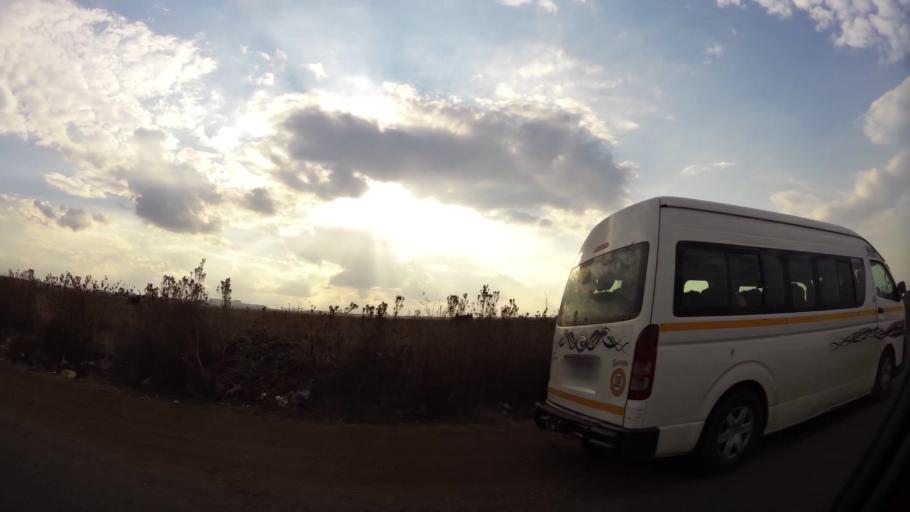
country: ZA
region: Gauteng
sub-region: Sedibeng District Municipality
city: Vereeniging
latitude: -26.6535
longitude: 27.8730
